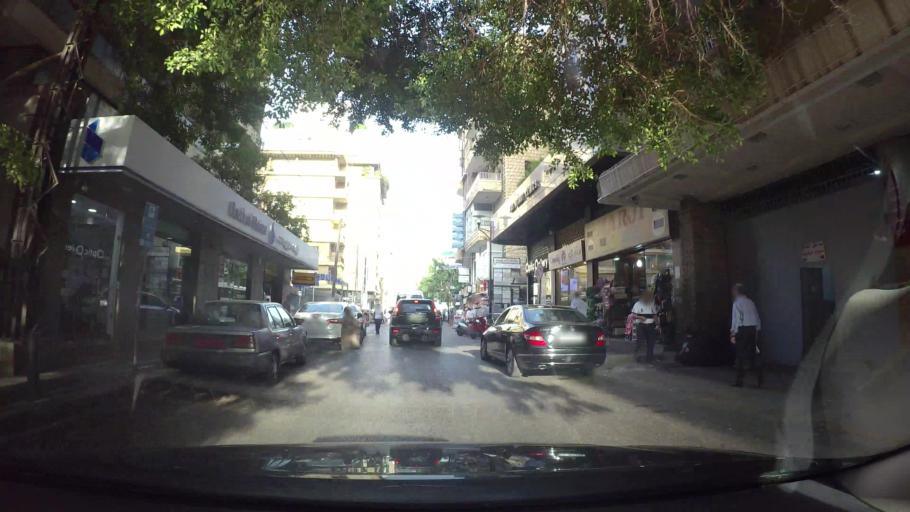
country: LB
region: Beyrouth
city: Ra's Bayrut
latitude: 33.8970
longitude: 35.4848
